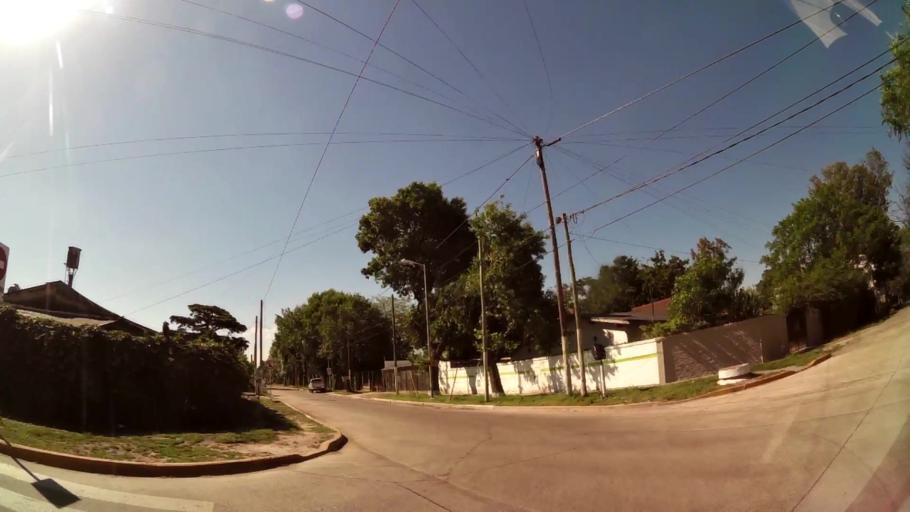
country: AR
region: Buenos Aires
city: Santa Catalina - Dique Lujan
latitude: -34.4906
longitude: -58.6923
